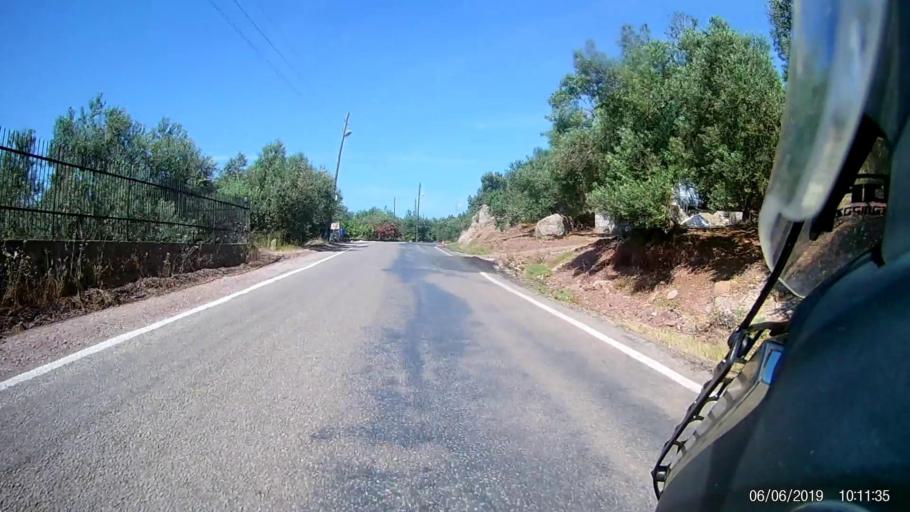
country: TR
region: Canakkale
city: Ayvacik
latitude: 39.5107
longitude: 26.4293
